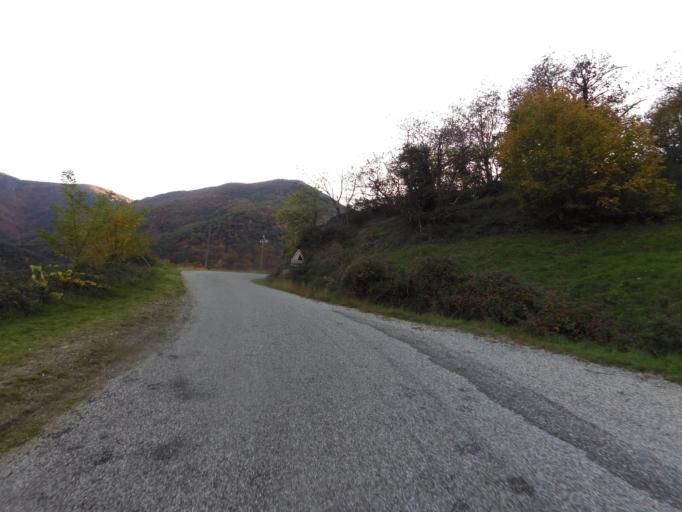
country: FR
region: Rhone-Alpes
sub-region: Departement de l'Ardeche
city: Les Vans
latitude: 44.5275
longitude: 4.0975
